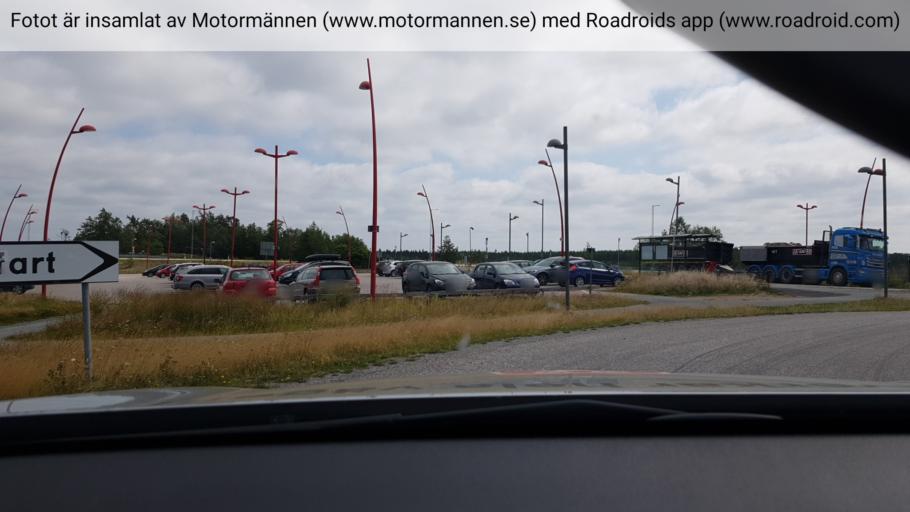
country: SE
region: Stockholm
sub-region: Norrtalje Kommun
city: Rimbo
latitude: 59.6351
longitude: 18.3311
